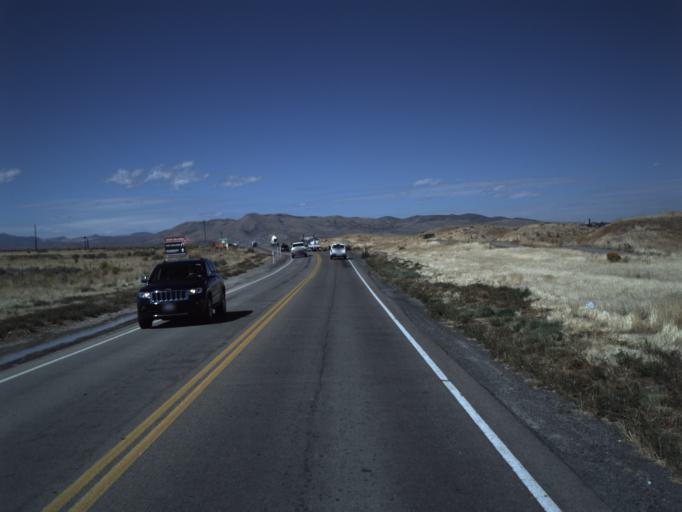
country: US
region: Utah
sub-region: Utah County
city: Saratoga Springs
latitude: 40.3234
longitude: -111.9033
